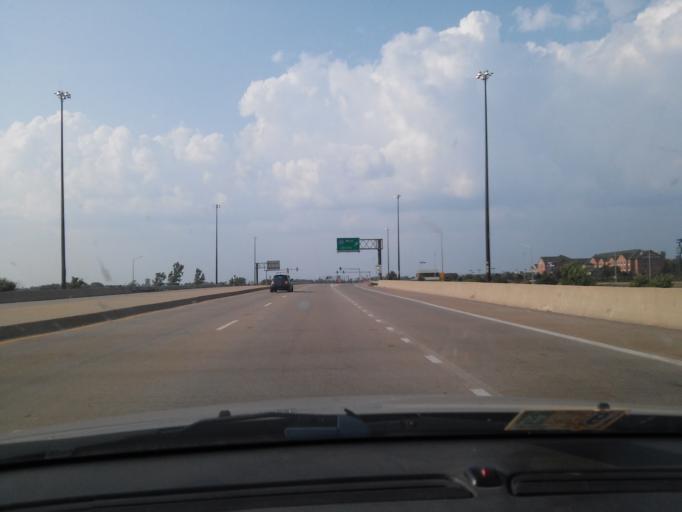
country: US
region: Illinois
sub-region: Cook County
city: Orland Hills
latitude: 41.5527
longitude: -87.8532
